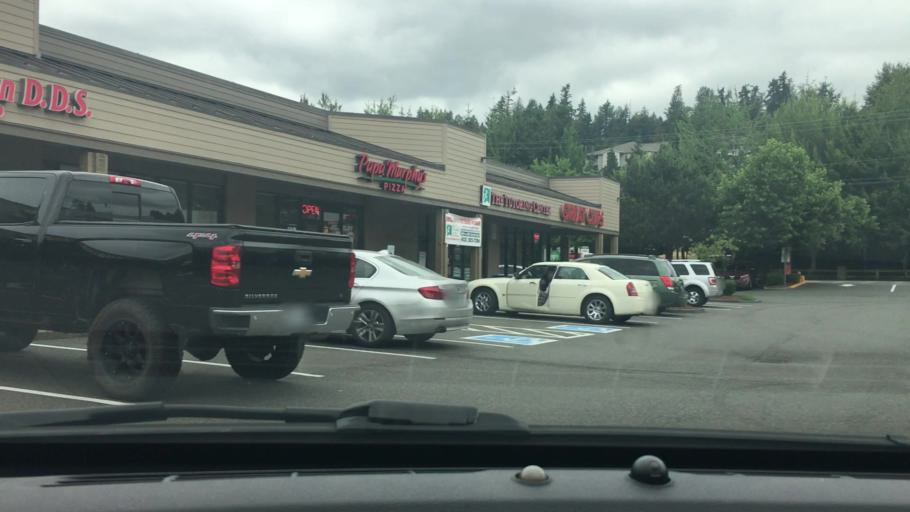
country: US
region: Washington
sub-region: King County
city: City of Sammamish
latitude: 47.6157
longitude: -122.0359
